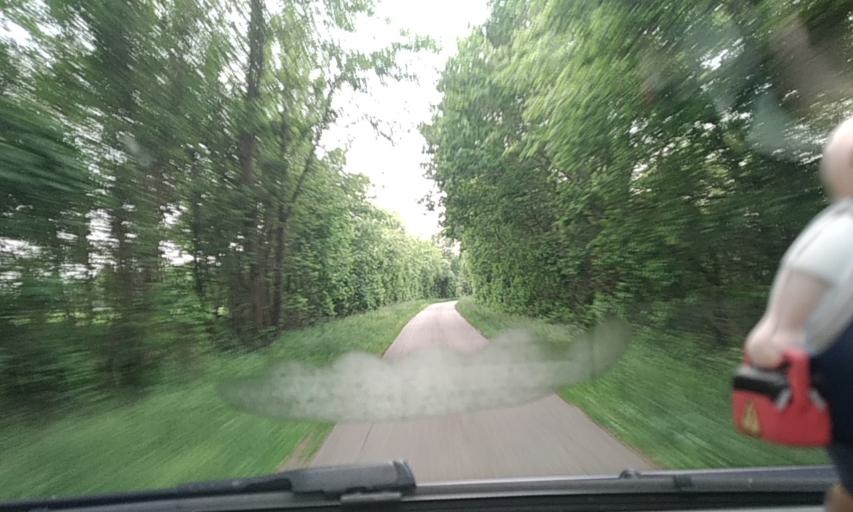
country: DE
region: Schleswig-Holstein
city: Borm
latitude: 54.3877
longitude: 9.4007
